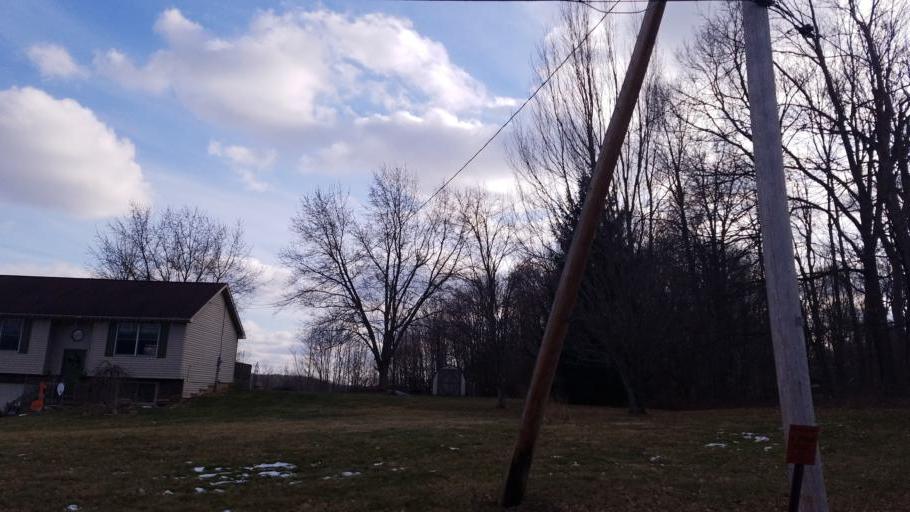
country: US
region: Ohio
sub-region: Crawford County
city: Crestline
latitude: 40.7183
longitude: -82.7079
